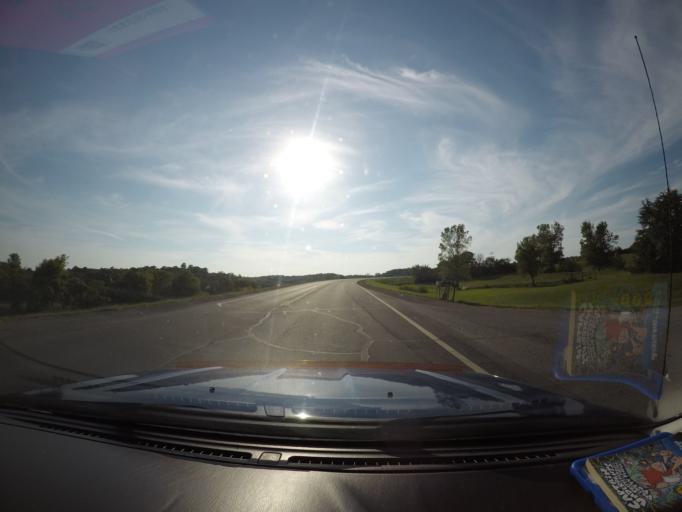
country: US
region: Kansas
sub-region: Atchison County
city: Atchison
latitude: 39.4848
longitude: -95.1216
